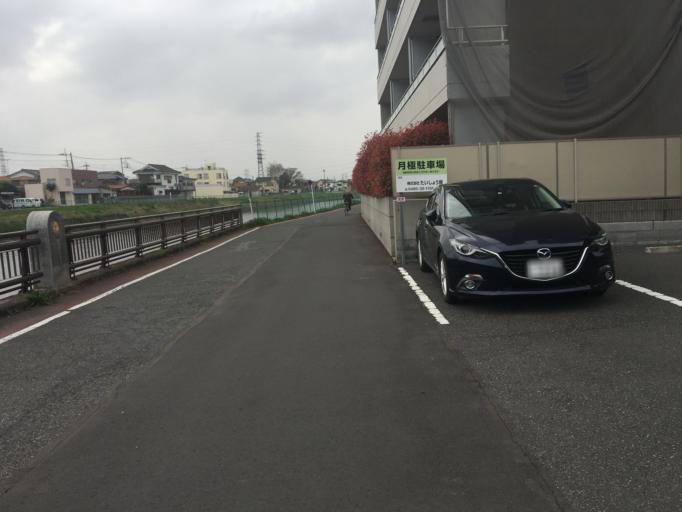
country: JP
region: Saitama
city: Sugito
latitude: 36.0267
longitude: 139.7267
